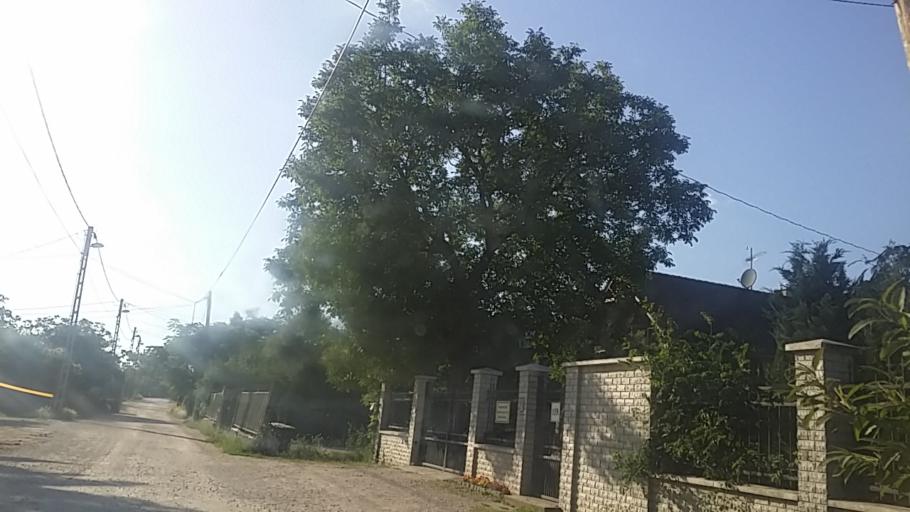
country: HU
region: Pest
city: Urom
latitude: 47.5817
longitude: 19.0063
